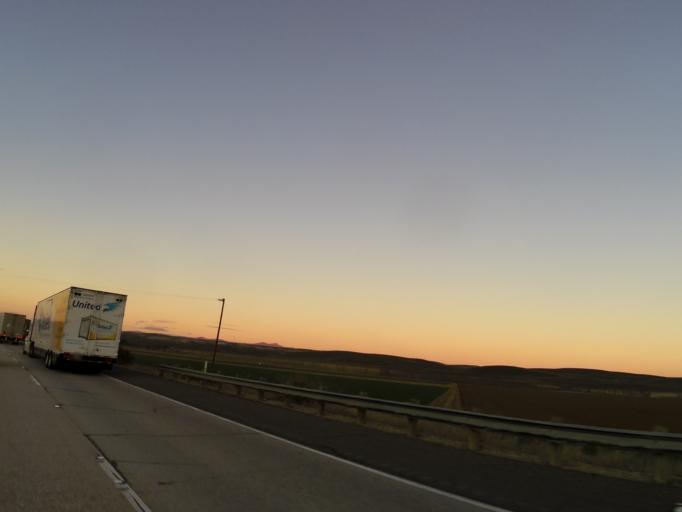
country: US
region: California
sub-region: Monterey County
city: King City
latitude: 36.1132
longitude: -121.0196
